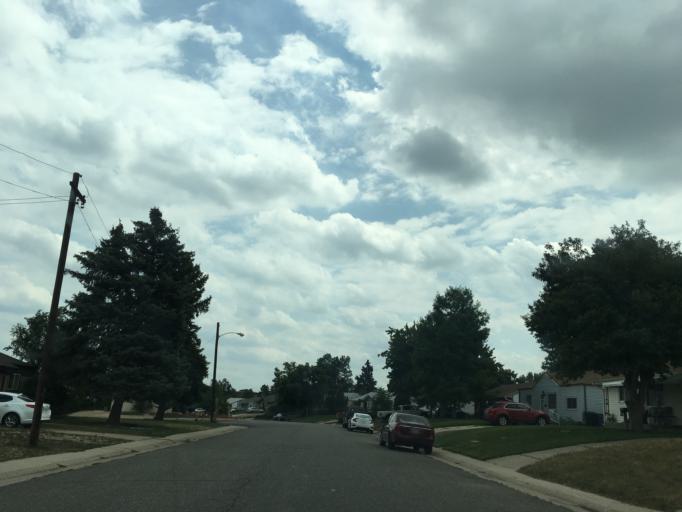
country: US
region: Colorado
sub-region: Arapahoe County
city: Sheridan
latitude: 39.6653
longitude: -105.0336
